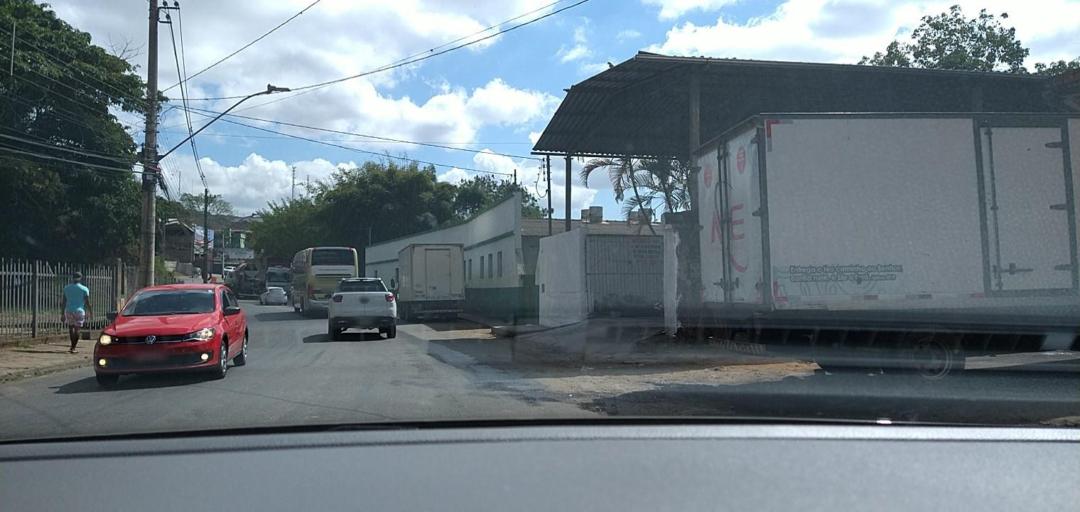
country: BR
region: Minas Gerais
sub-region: Ponte Nova
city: Ponte Nova
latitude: -20.4200
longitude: -42.8989
